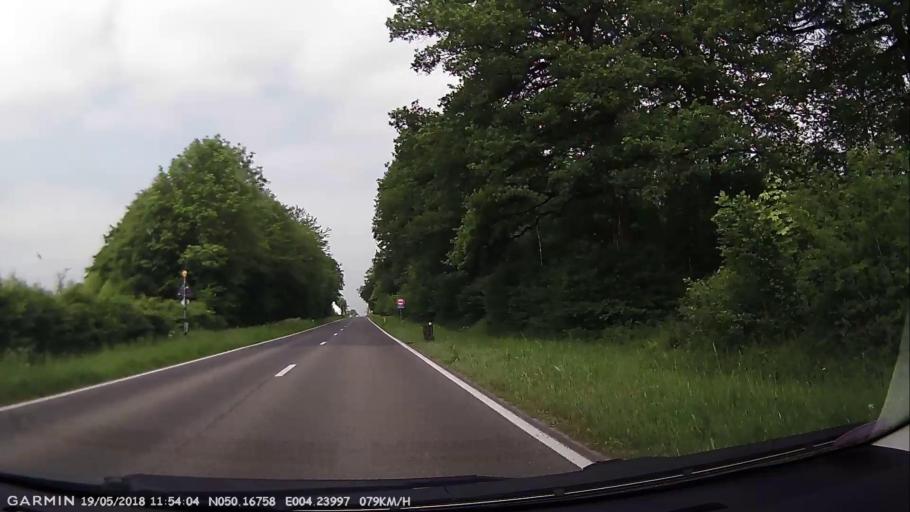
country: BE
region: Wallonia
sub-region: Province du Hainaut
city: Beaumont
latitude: 50.1678
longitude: 4.2397
